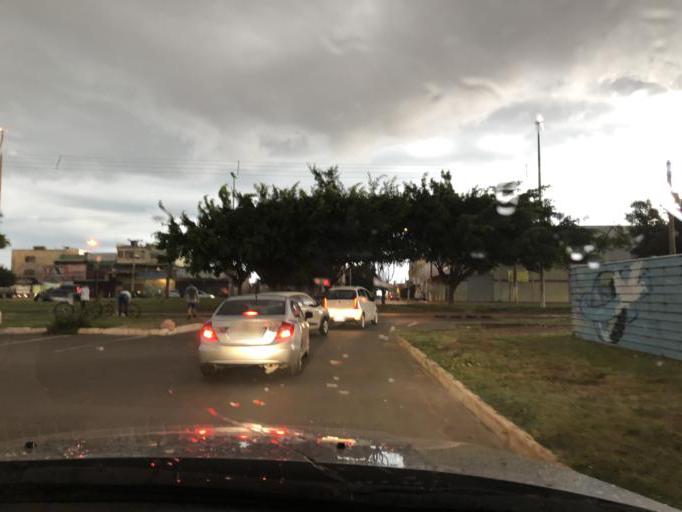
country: BR
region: Federal District
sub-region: Brasilia
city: Brasilia
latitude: -15.8045
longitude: -48.1113
